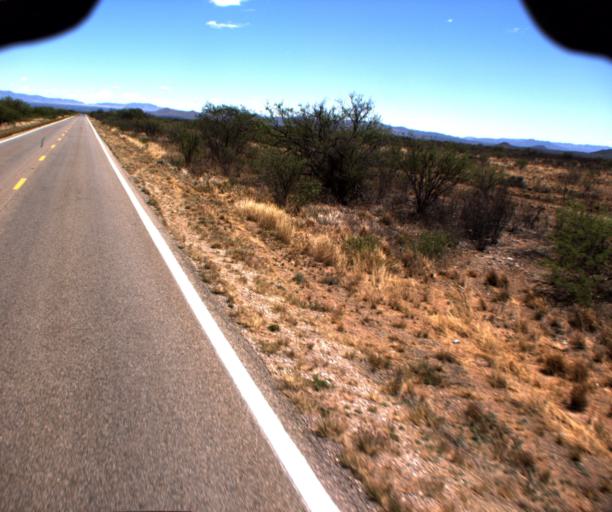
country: US
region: Arizona
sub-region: Cochise County
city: Huachuca City
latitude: 31.7089
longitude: -110.2781
